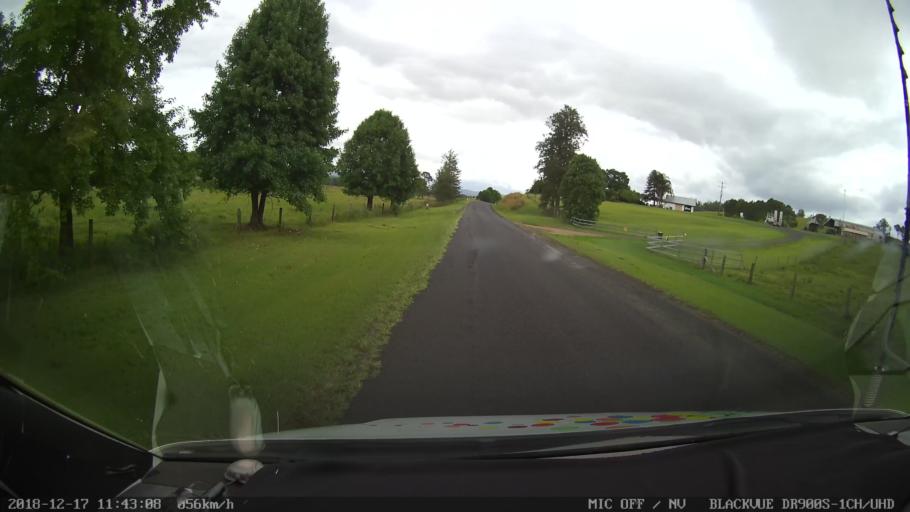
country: AU
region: New South Wales
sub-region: Kyogle
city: Kyogle
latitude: -28.6628
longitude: 152.5927
